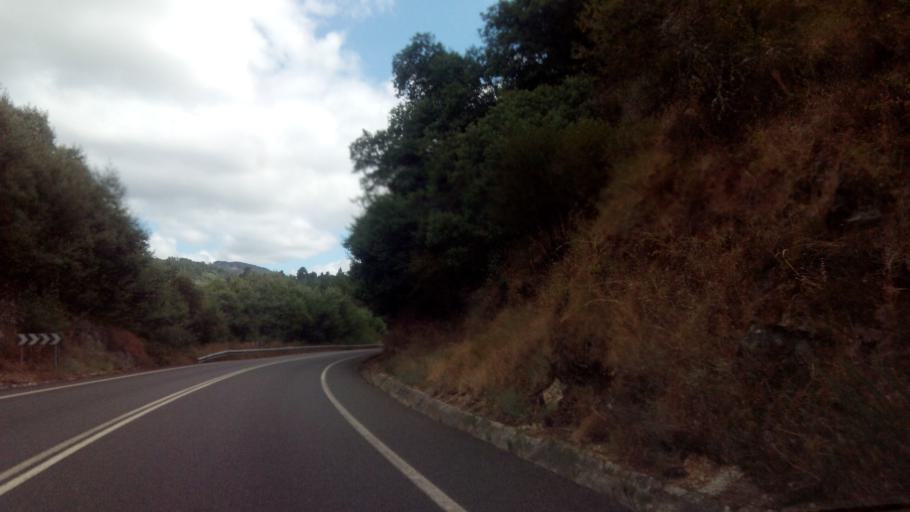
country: ES
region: Galicia
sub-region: Provincia de Ourense
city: Coles
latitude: 42.4004
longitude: -7.7996
